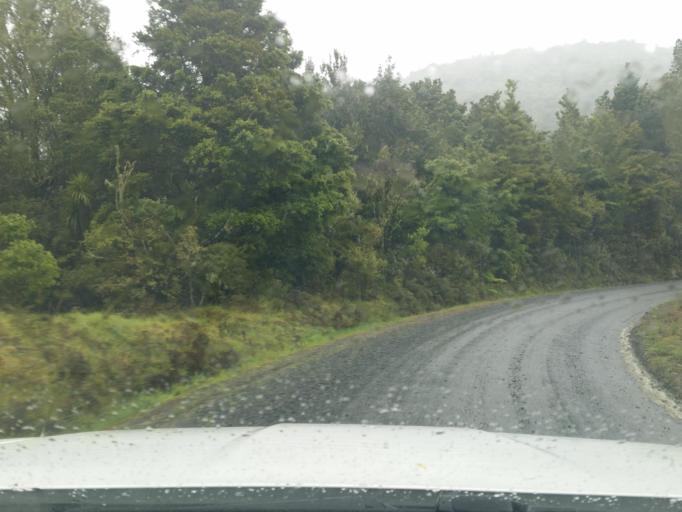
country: NZ
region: Northland
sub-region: Kaipara District
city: Dargaville
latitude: -35.7558
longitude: 173.9577
